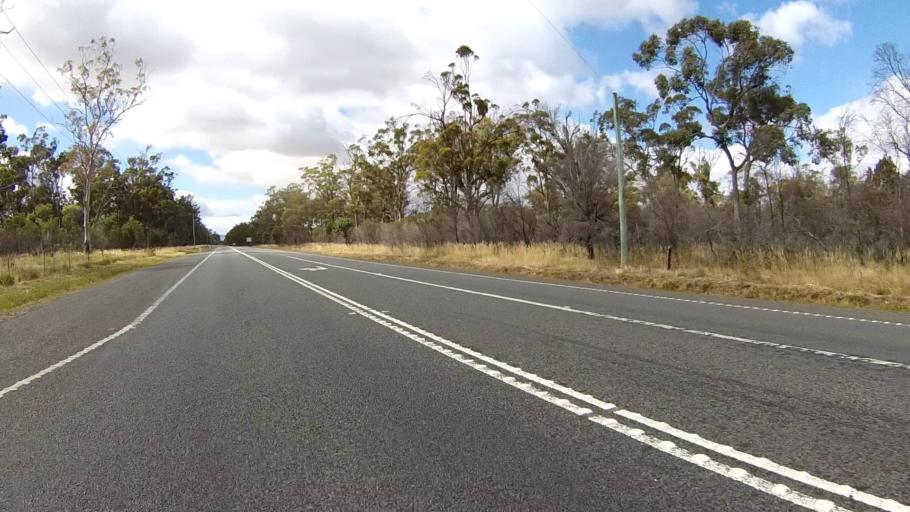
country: AU
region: Tasmania
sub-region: Northern Midlands
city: Evandale
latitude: -41.8199
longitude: 147.4234
